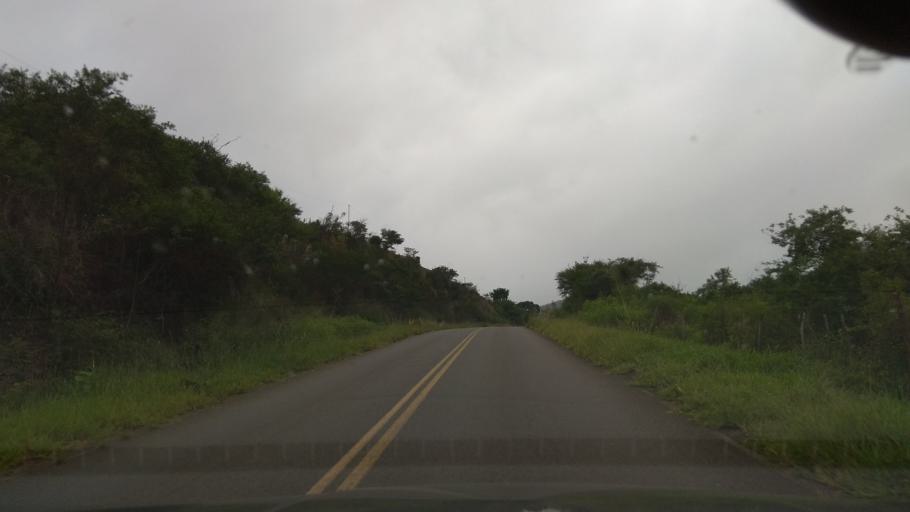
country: BR
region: Bahia
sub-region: Santa Ines
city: Santa Ines
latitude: -13.2425
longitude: -39.7592
